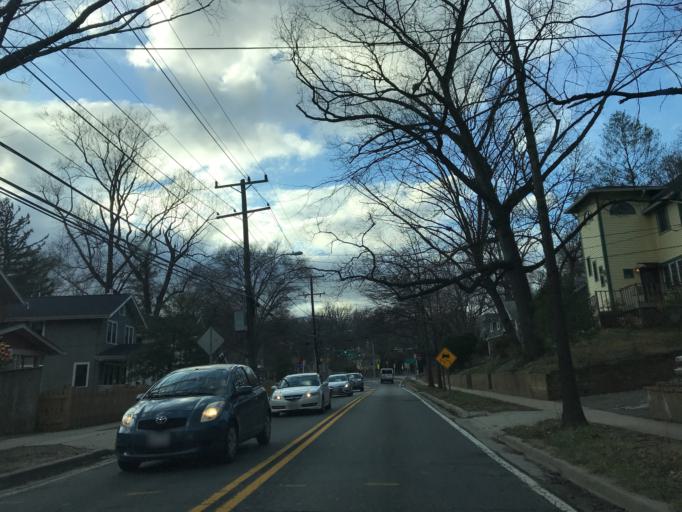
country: US
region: Maryland
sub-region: Montgomery County
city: Takoma Park
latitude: 38.9825
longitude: -77.0140
